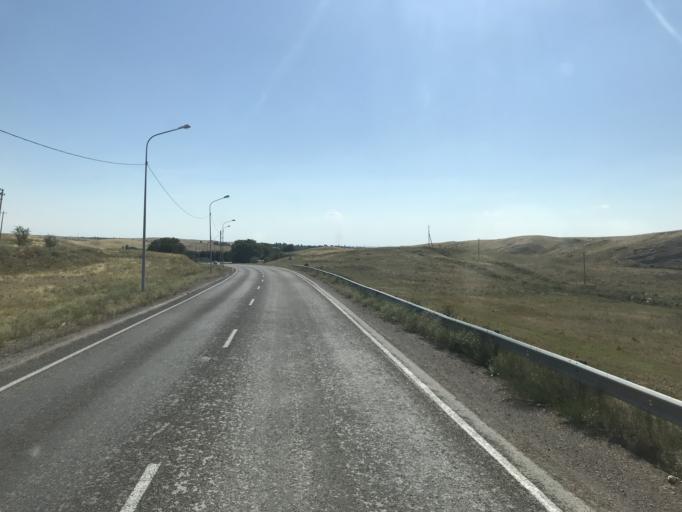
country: KZ
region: Zhambyl
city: Georgiyevka
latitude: 43.2433
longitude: 74.7808
